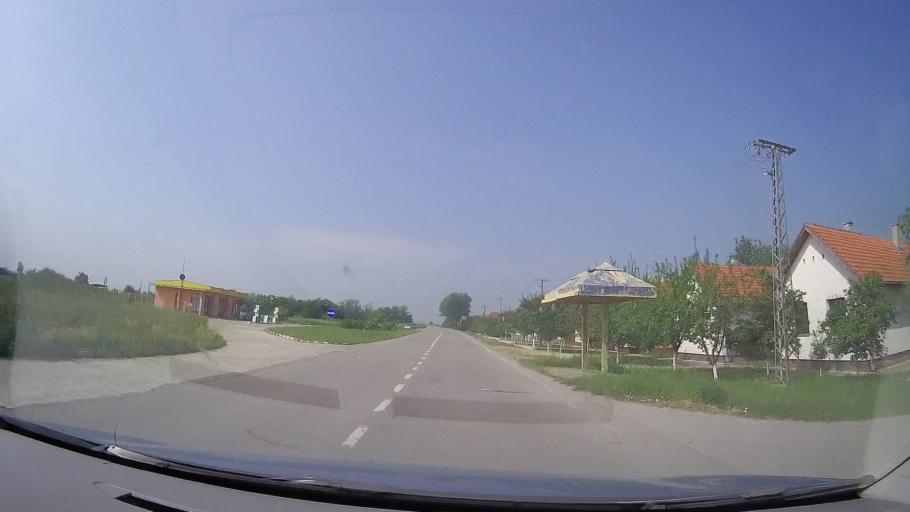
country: RS
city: Jasa Tomic
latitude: 45.4339
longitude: 20.8437
